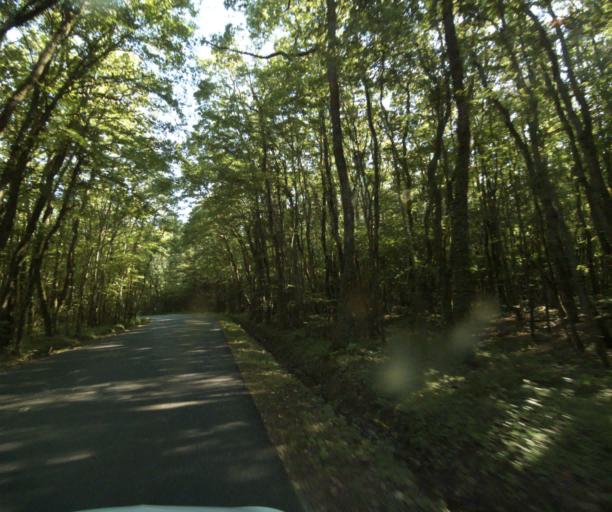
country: FR
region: Rhone-Alpes
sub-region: Departement de la Haute-Savoie
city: Massongy
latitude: 46.3374
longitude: 6.3264
